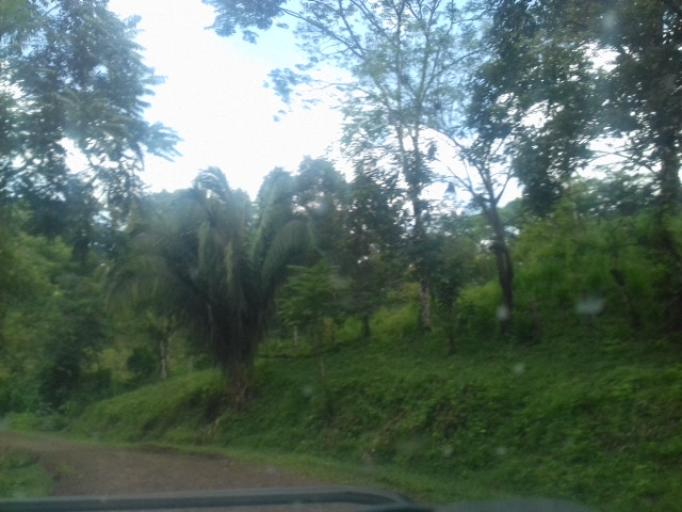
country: NI
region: Matagalpa
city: Matiguas
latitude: 12.9220
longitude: -85.3651
